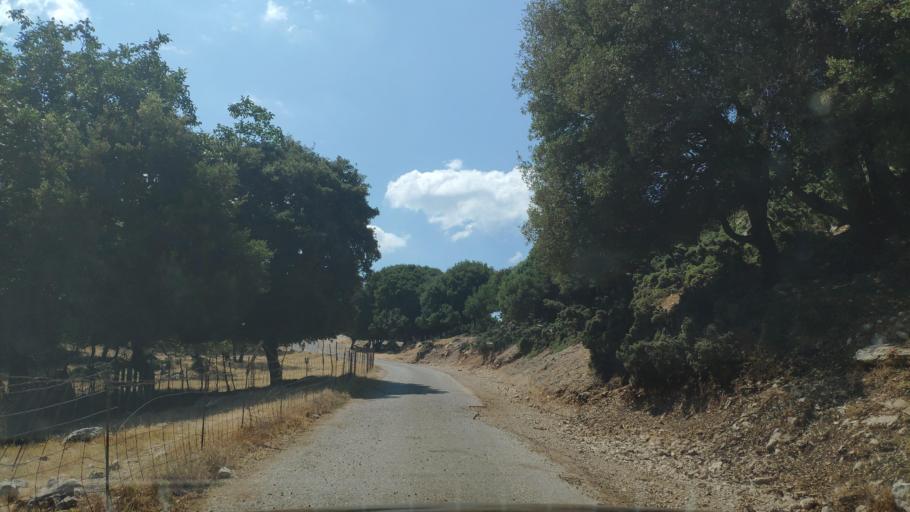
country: GR
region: West Greece
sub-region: Nomos Aitolias kai Akarnanias
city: Monastirakion
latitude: 38.8044
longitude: 20.9463
